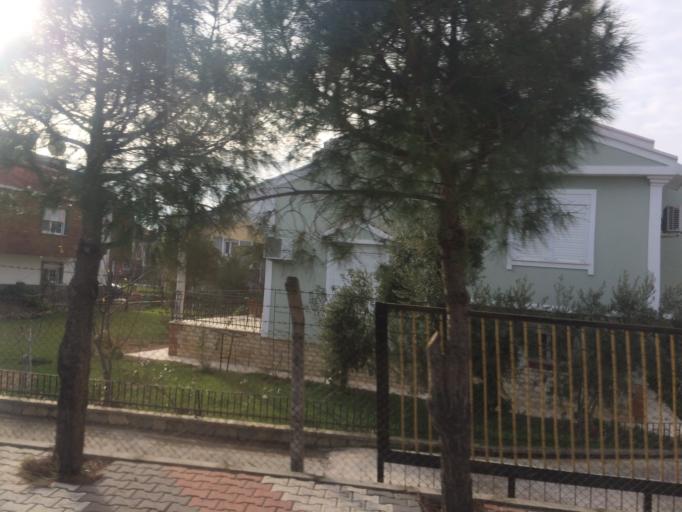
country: TR
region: Izmir
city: Menemen
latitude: 38.5053
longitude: 26.9587
